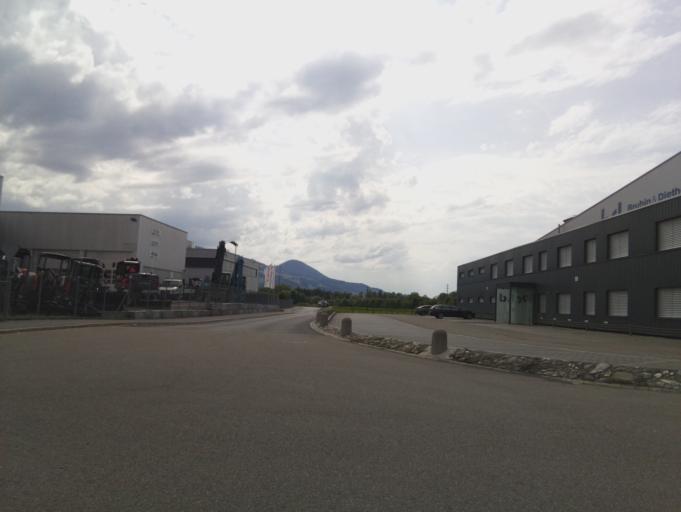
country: CH
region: Schwyz
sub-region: Bezirk March
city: Lachen
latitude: 47.1958
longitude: 8.8797
